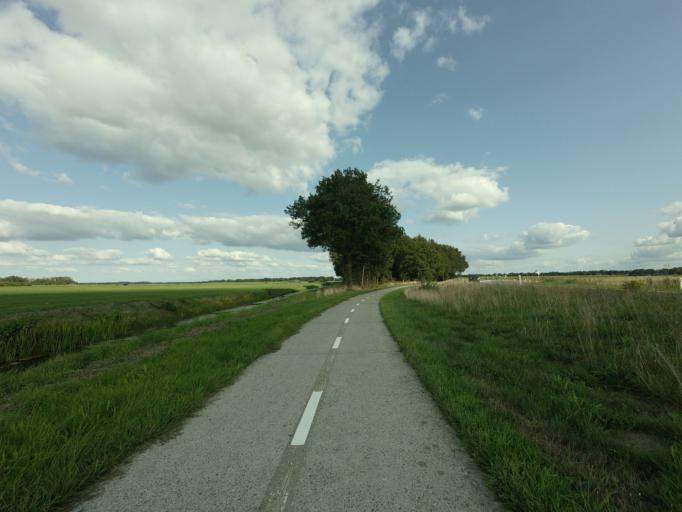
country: NL
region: Drenthe
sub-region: Gemeente Westerveld
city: Dwingeloo
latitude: 52.8395
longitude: 6.3959
